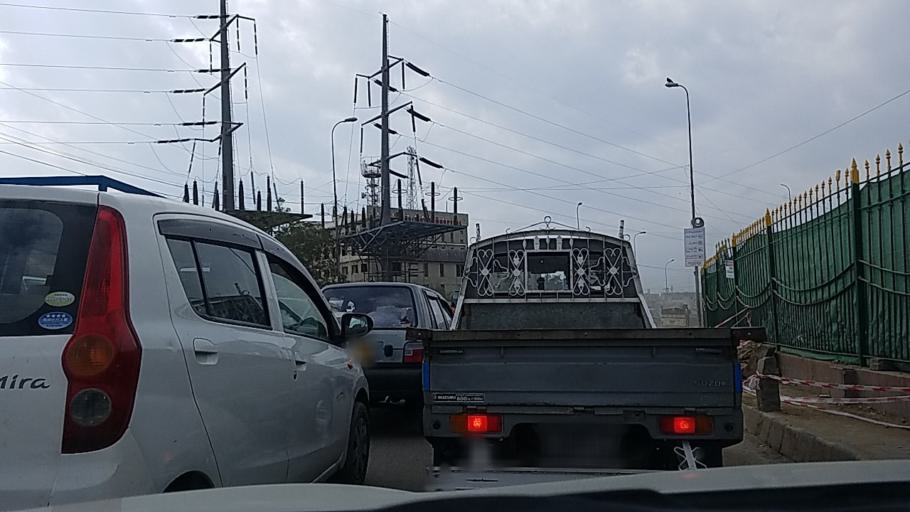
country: PK
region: Sindh
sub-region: Karachi District
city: Karachi
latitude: 24.8295
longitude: 67.0805
